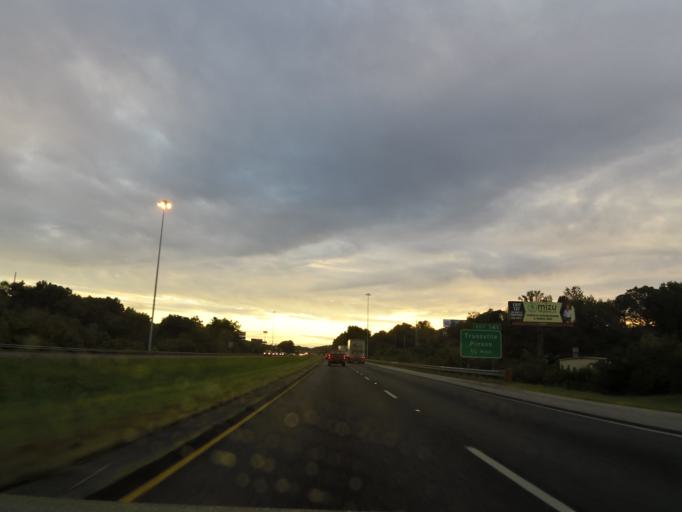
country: US
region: Alabama
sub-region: Jefferson County
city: Trussville
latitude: 33.6469
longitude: -86.6105
